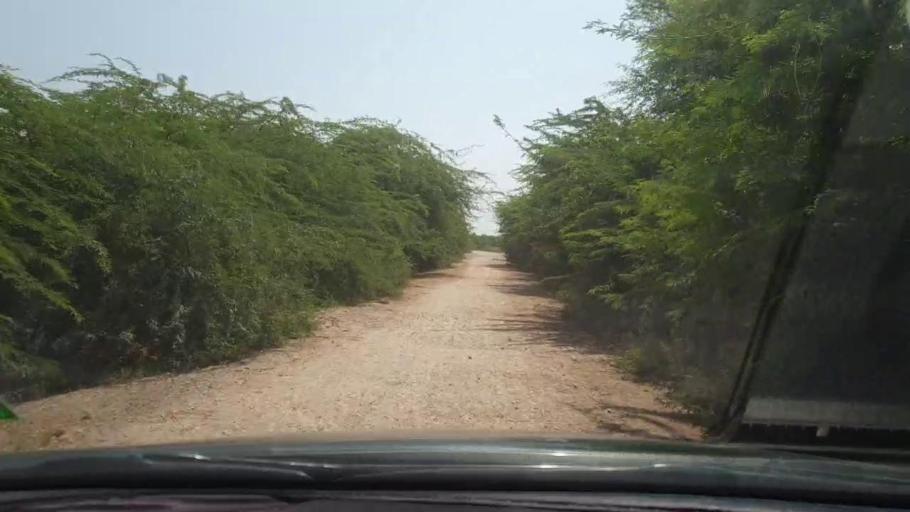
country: PK
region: Sindh
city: Tando Bago
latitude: 24.7866
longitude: 69.1731
